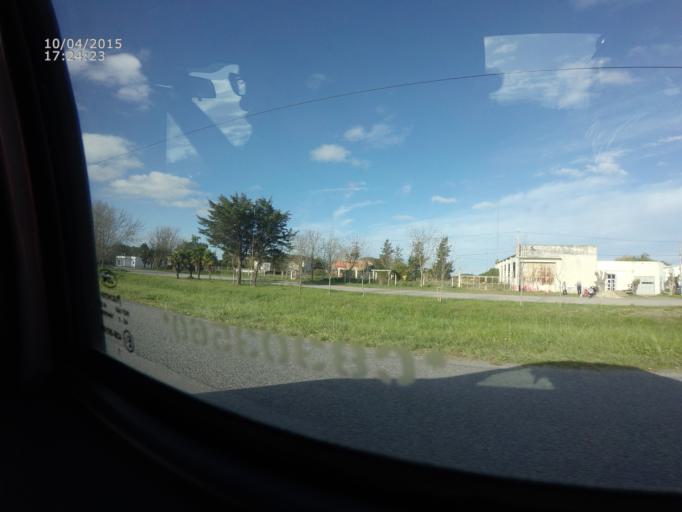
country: AR
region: Buenos Aires
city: Maipu
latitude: -37.0867
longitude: -57.8281
